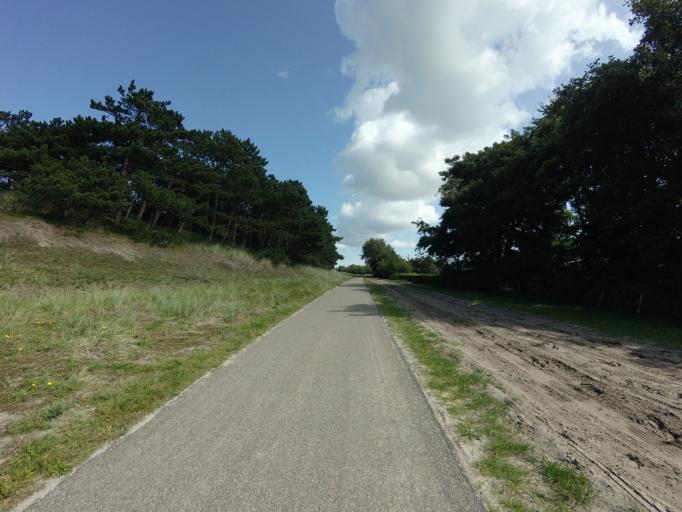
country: NL
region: Friesland
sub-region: Gemeente Terschelling
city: West-Terschelling
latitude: 53.3978
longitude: 5.3368
